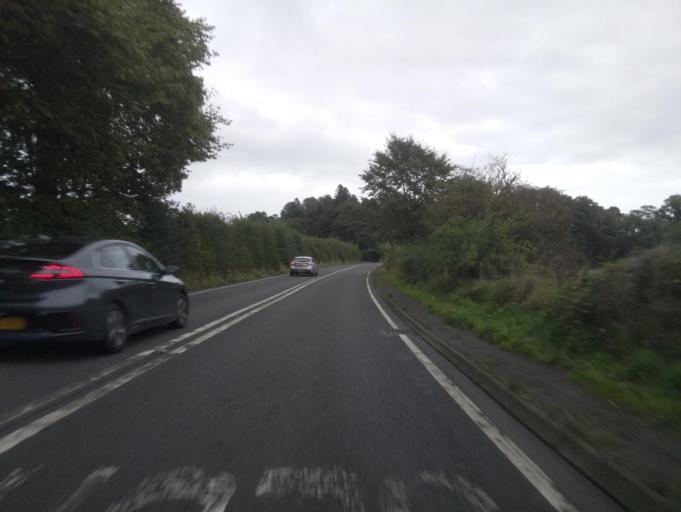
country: GB
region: Scotland
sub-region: Clackmannanshire
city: Tillicoultry
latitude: 56.1589
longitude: -3.7067
